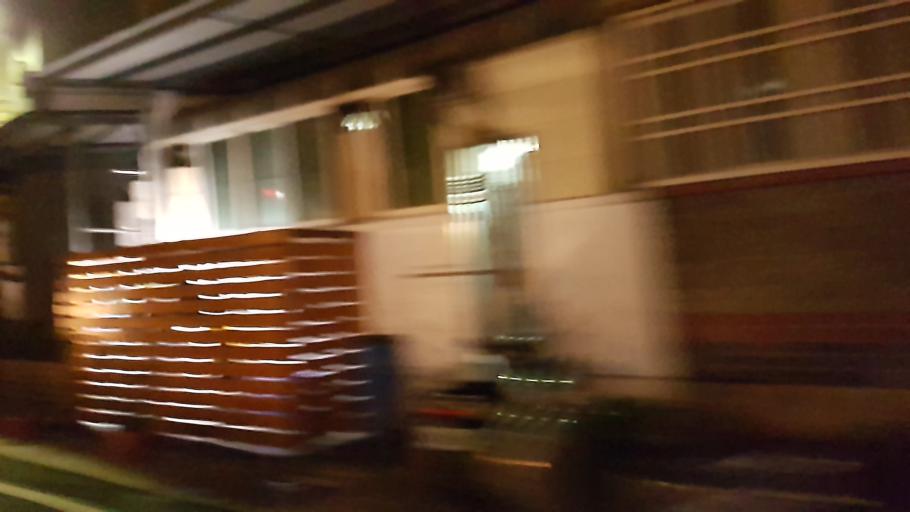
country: TW
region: Taiwan
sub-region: Hsinchu
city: Hsinchu
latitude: 24.7980
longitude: 120.9513
